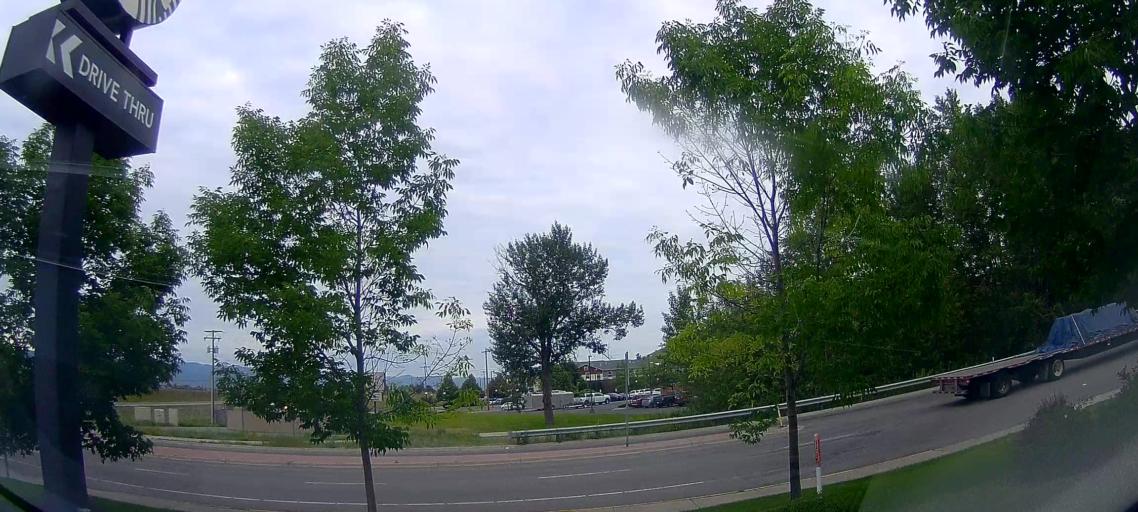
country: US
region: Montana
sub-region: Missoula County
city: Orchard Homes
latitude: 46.9144
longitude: -114.0333
